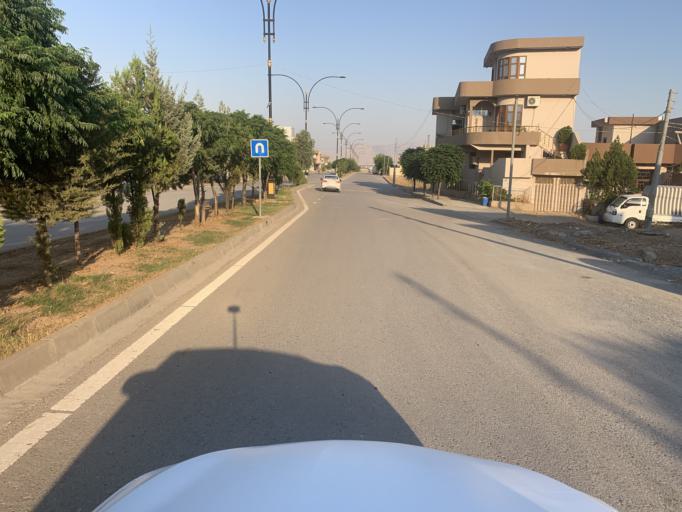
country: IQ
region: As Sulaymaniyah
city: Raniye
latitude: 36.2392
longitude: 44.8781
